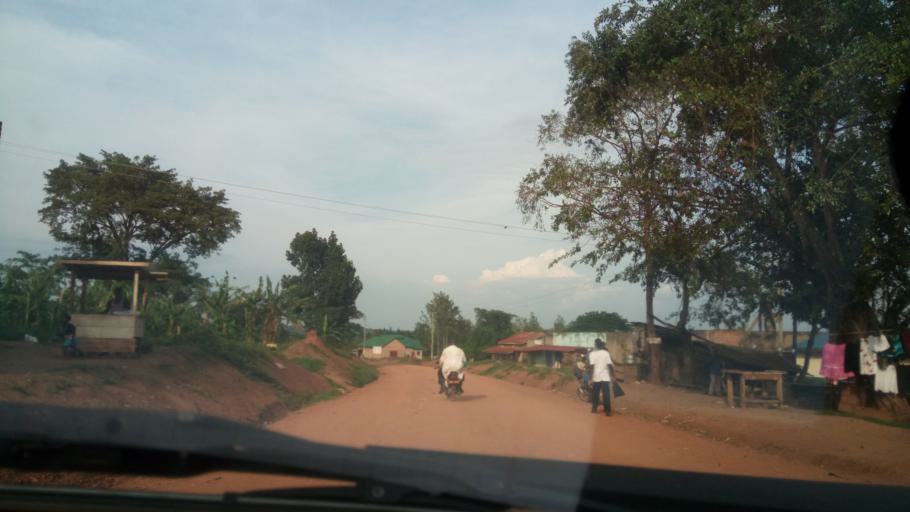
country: UG
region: Central Region
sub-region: Mityana District
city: Mityana
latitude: 0.5009
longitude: 32.1386
